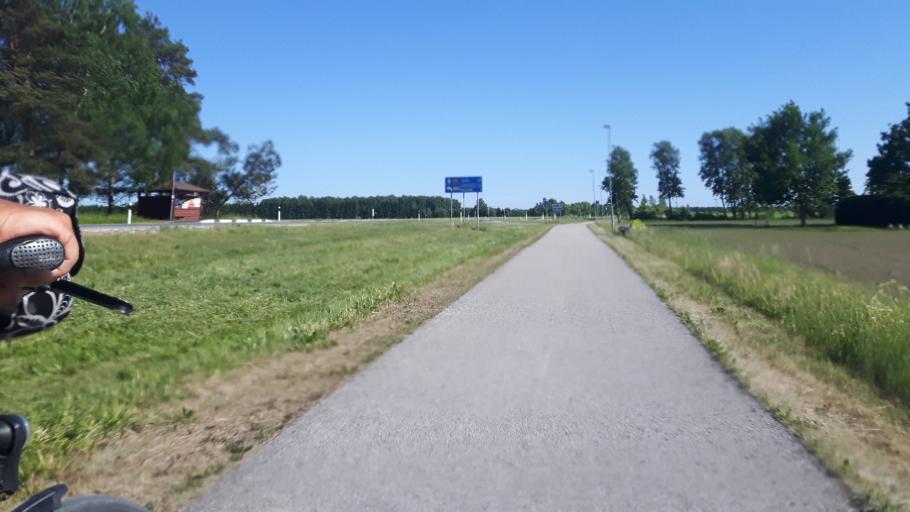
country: EE
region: Raplamaa
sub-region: Kehtna vald
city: Kehtna
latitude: 58.9418
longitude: 24.8788
